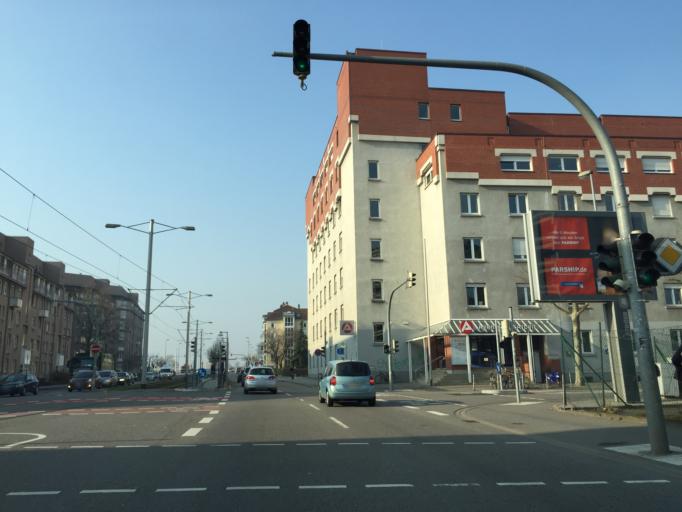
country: DE
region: Baden-Wuerttemberg
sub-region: Karlsruhe Region
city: Heidelberg
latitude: 49.4036
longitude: 8.6817
